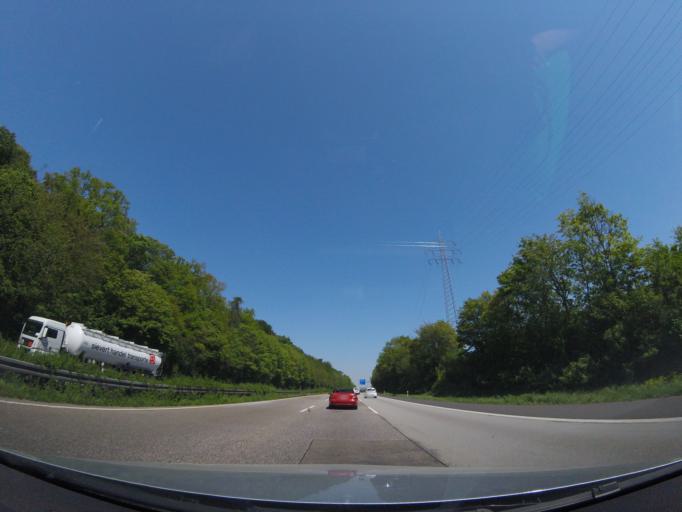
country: DE
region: Hesse
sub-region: Regierungsbezirk Darmstadt
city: Offenbach
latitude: 50.0859
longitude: 8.7374
